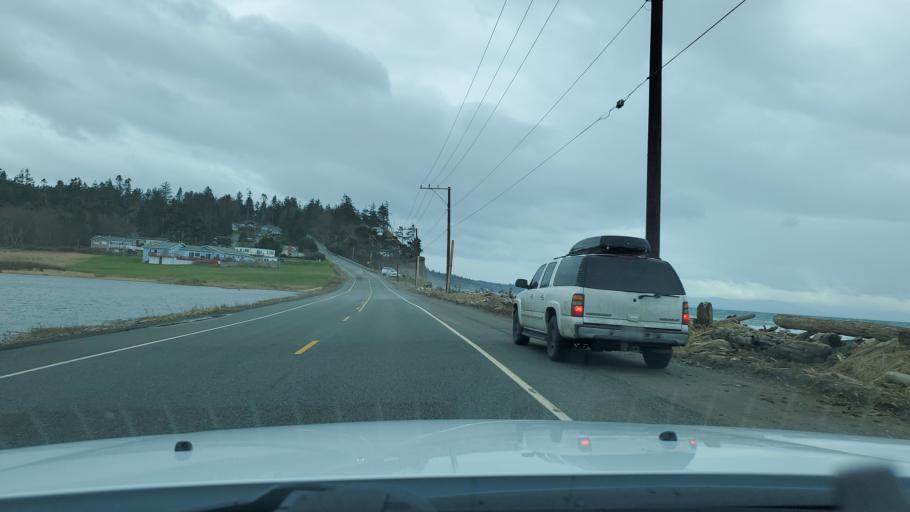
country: US
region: Washington
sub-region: Island County
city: Ault Field
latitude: 48.2998
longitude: -122.7242
